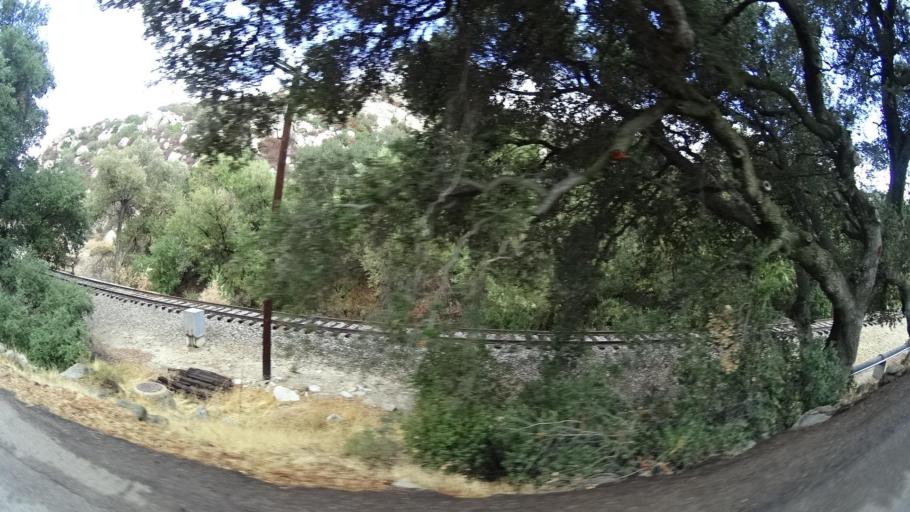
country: US
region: California
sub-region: San Diego County
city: Campo
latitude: 32.6079
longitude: -116.4757
